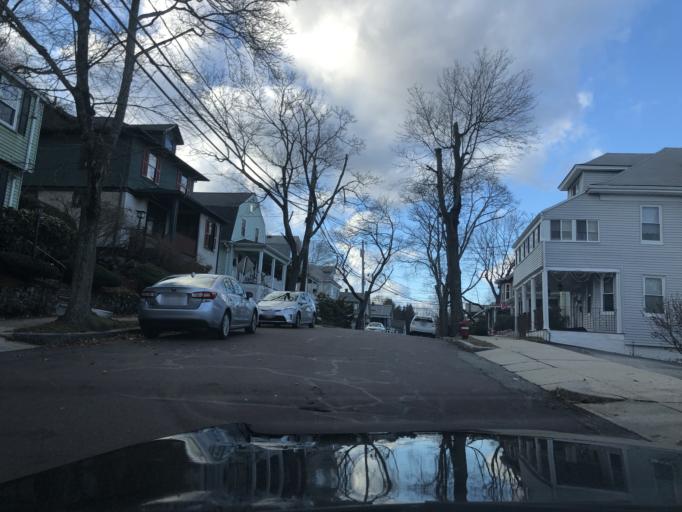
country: US
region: Massachusetts
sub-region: Middlesex County
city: Arlington
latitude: 42.4166
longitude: -71.1649
